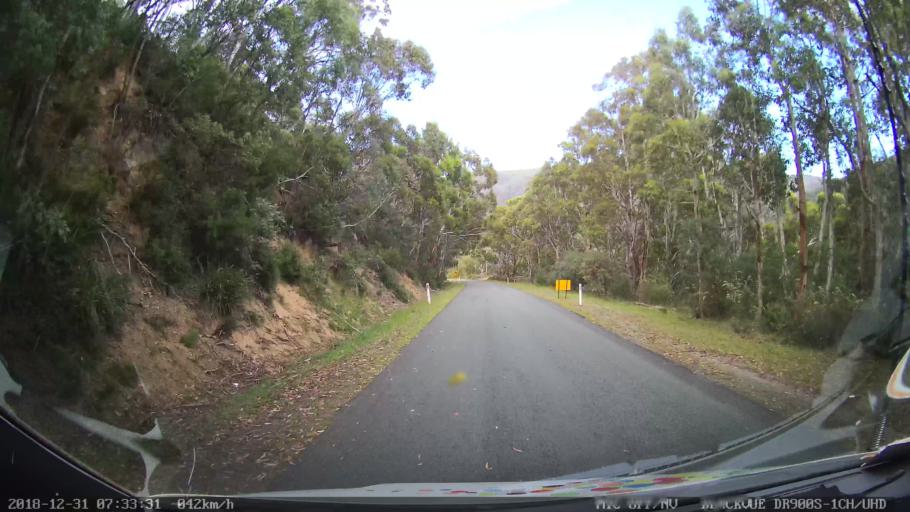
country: AU
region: New South Wales
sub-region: Snowy River
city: Jindabyne
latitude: -36.3329
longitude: 148.4566
